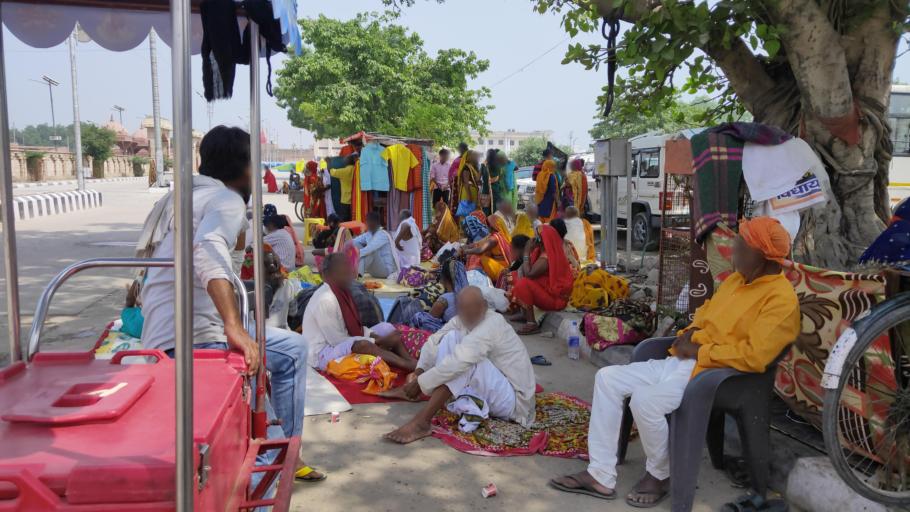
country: IN
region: Uttar Pradesh
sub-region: Faizabad
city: Ayodhya
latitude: 26.8083
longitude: 82.2109
